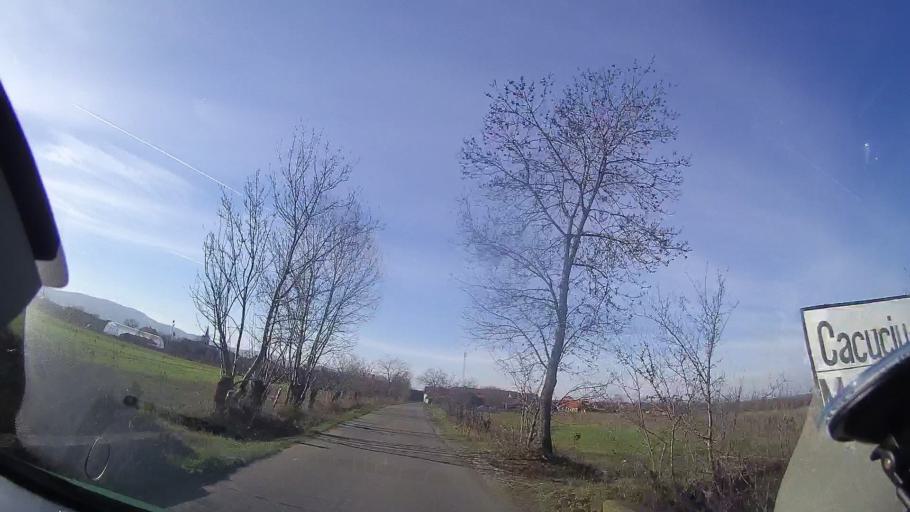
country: RO
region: Bihor
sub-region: Comuna Auseu
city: Grosi
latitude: 47.0275
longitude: 22.4769
